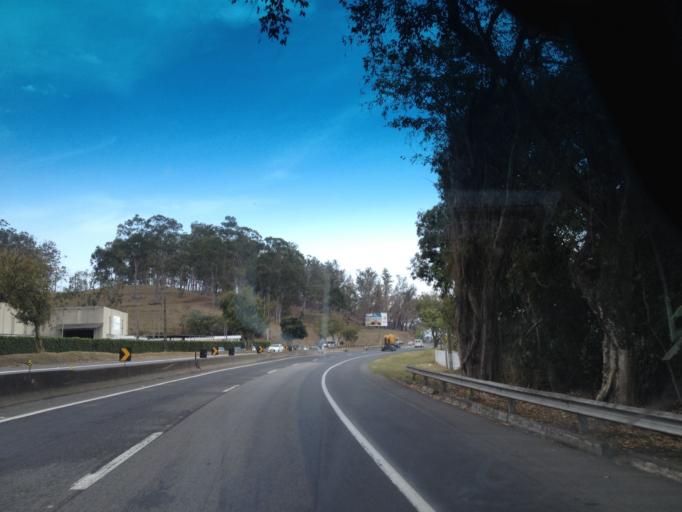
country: BR
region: Rio de Janeiro
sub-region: Porto Real
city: Porto Real
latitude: -22.4616
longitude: -44.2896
